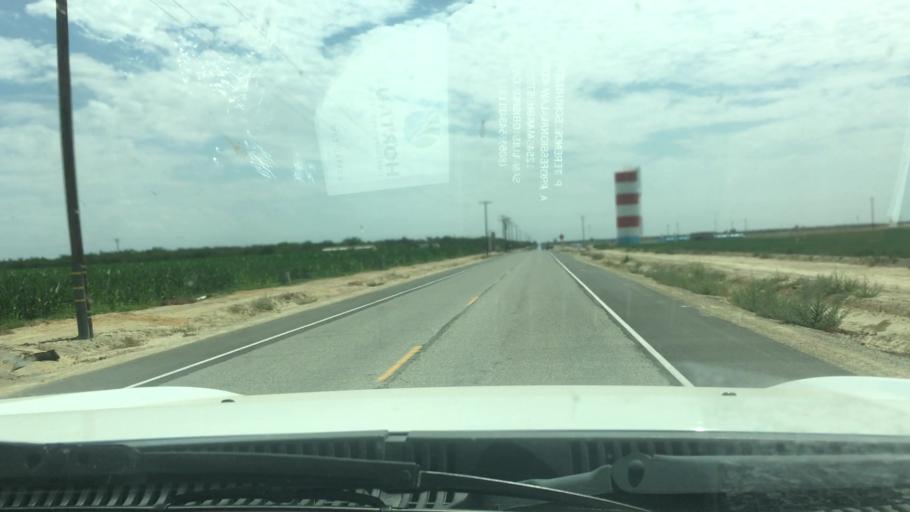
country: US
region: California
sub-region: Kern County
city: Wasco
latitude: 35.5579
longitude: -119.4061
